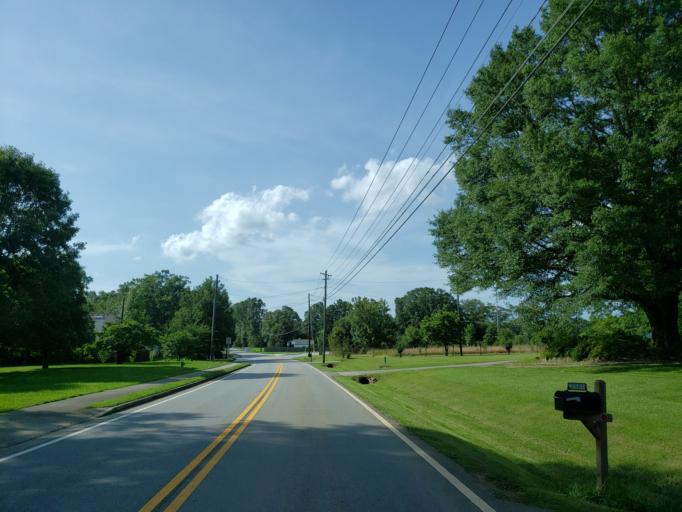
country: US
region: Georgia
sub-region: Cobb County
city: Powder Springs
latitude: 33.8906
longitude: -84.6846
